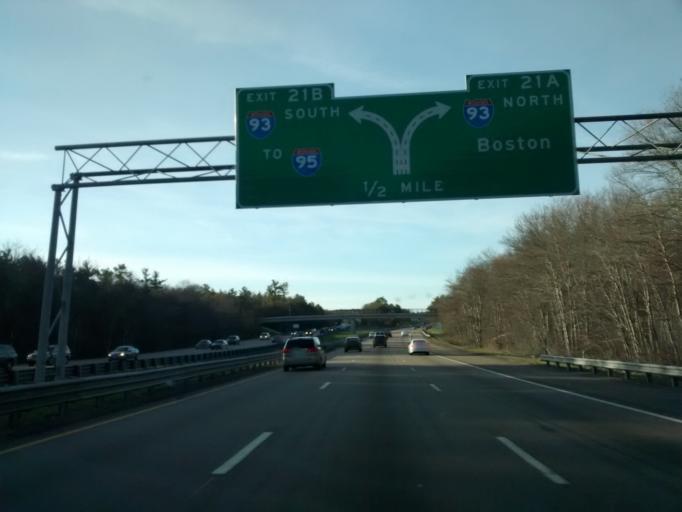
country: US
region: Massachusetts
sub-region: Norfolk County
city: Randolph
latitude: 42.1911
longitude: -71.0773
